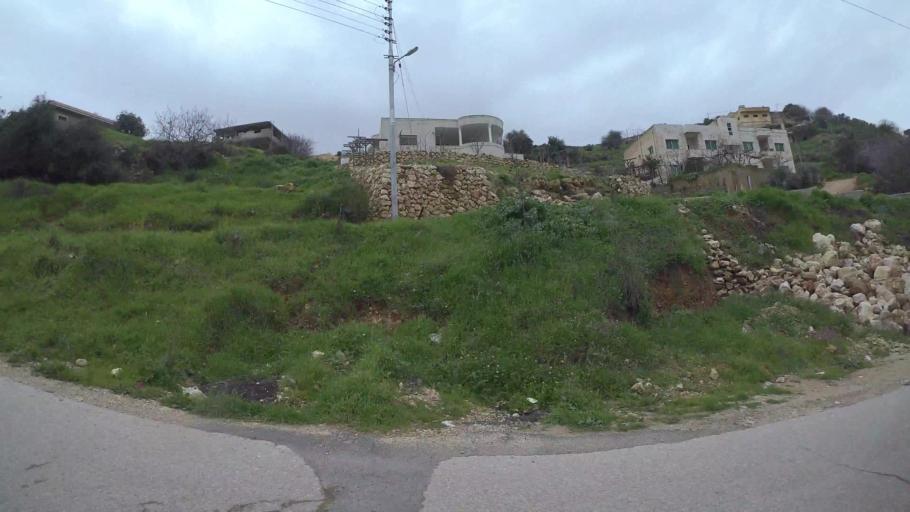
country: JO
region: Amman
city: Wadi as Sir
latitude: 31.9600
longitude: 35.8113
